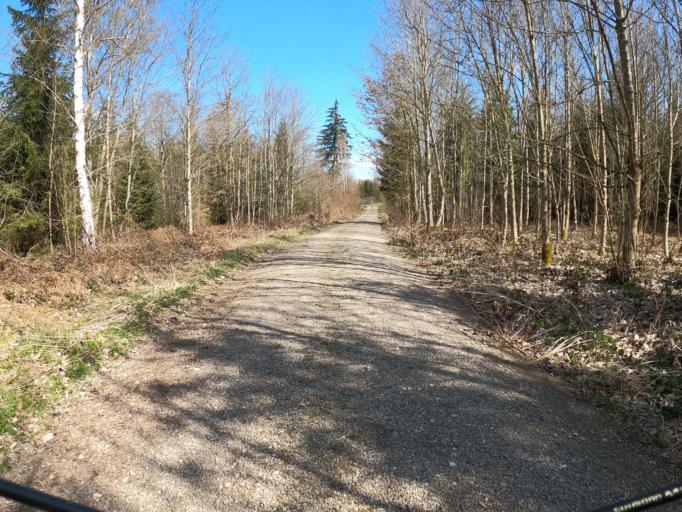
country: DE
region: Bavaria
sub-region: Swabia
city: Nersingen
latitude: 48.4045
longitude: 10.1589
